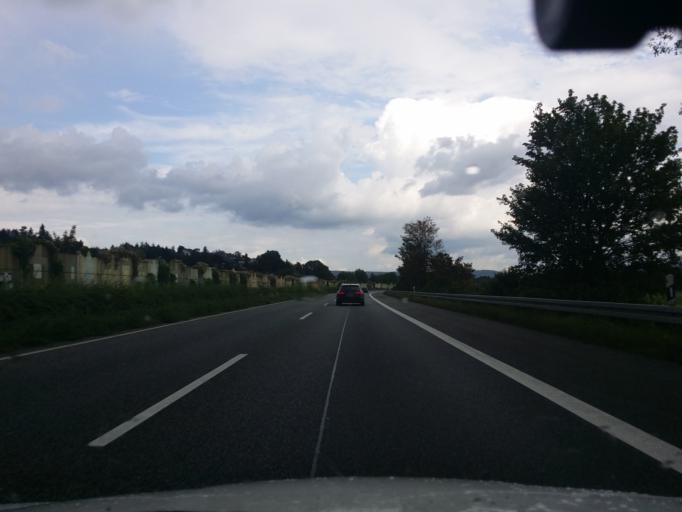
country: DE
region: Hesse
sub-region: Regierungsbezirk Darmstadt
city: Langenselbold
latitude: 50.1914
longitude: 9.0964
